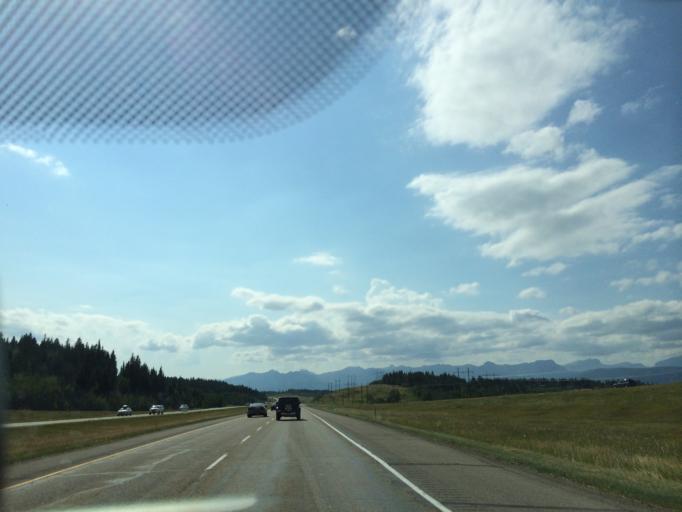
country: CA
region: Alberta
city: Cochrane
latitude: 51.1479
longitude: -114.8437
